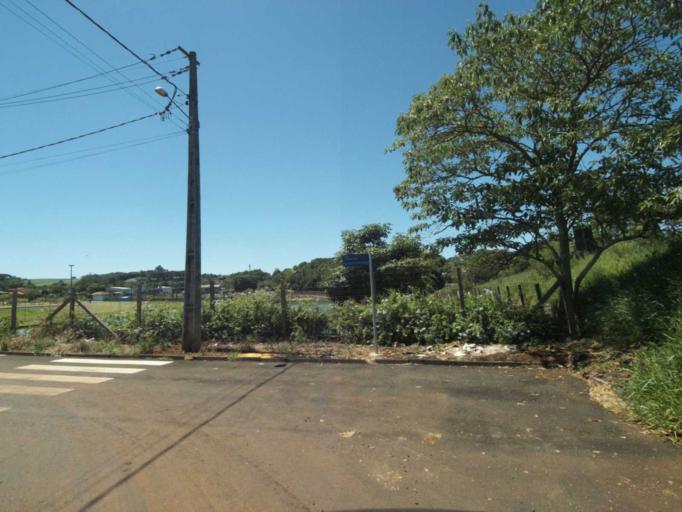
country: BR
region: Parana
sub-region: Coronel Vivida
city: Coronel Vivida
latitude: -25.9813
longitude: -52.8127
